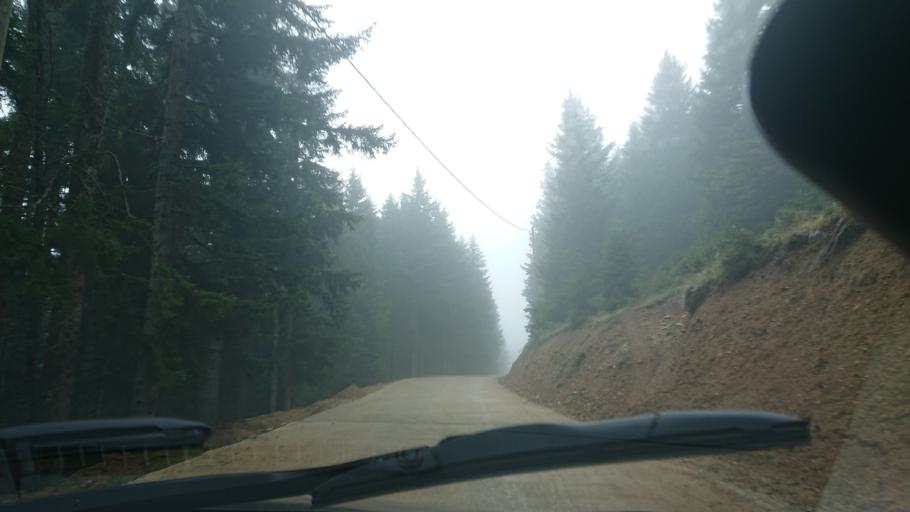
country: TR
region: Gumushane
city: Kurtun
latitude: 40.6706
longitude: 39.0030
